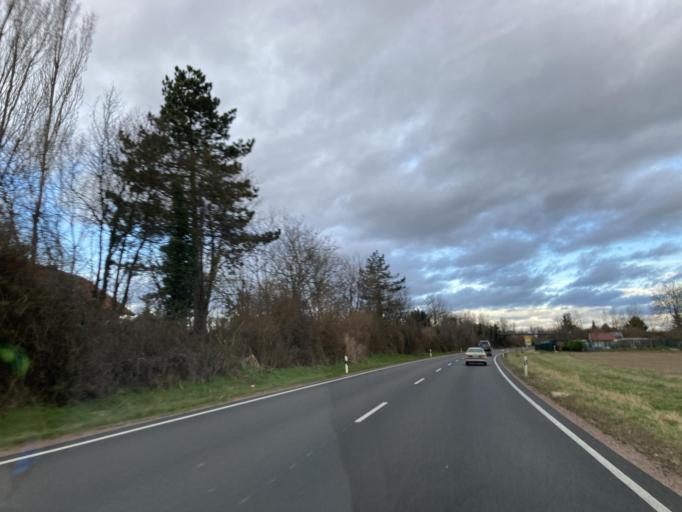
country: DE
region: Baden-Wuerttemberg
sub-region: Freiburg Region
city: Breisach am Rhein
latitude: 48.0399
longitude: 7.5886
